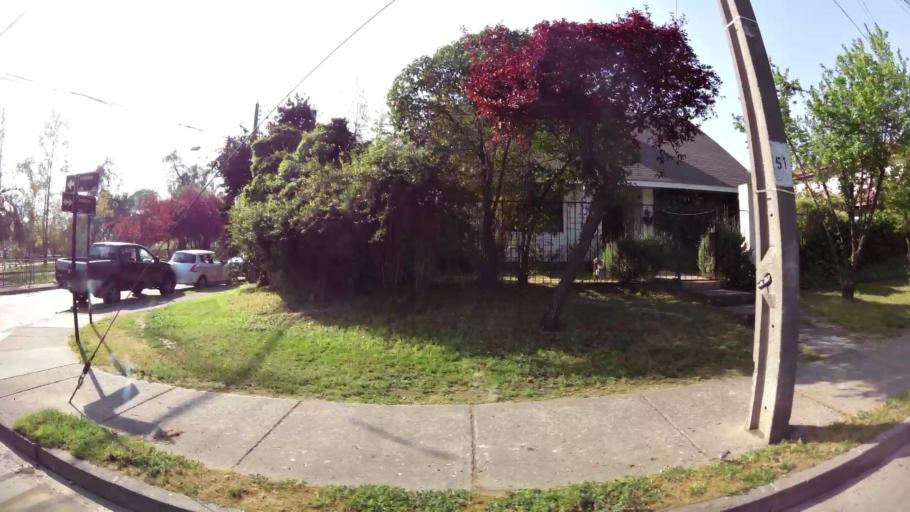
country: CL
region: Santiago Metropolitan
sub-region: Provincia de Santiago
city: Villa Presidente Frei, Nunoa, Santiago, Chile
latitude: -33.3829
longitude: -70.5577
